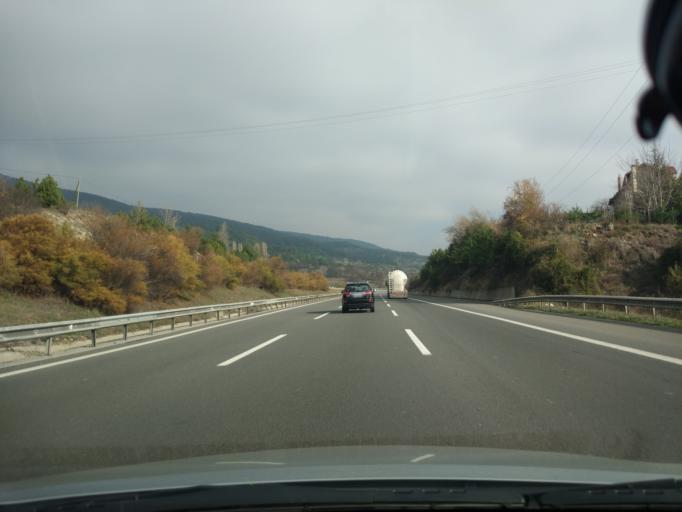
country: TR
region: Bolu
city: Bolu
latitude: 40.7585
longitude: 31.5835
